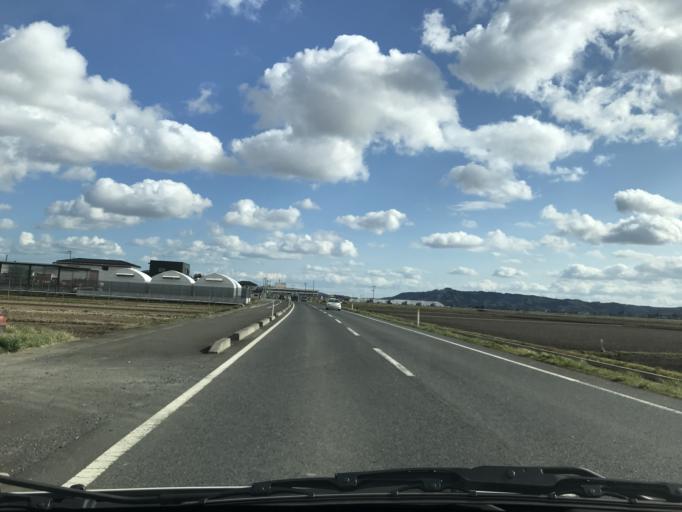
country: JP
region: Miyagi
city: Wakuya
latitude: 38.6352
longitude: 141.1876
